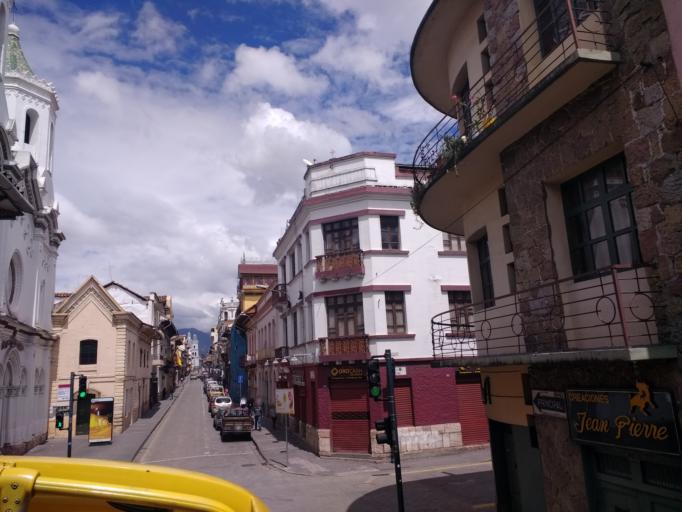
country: EC
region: Azuay
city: Cuenca
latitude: -2.8961
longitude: -79.0076
